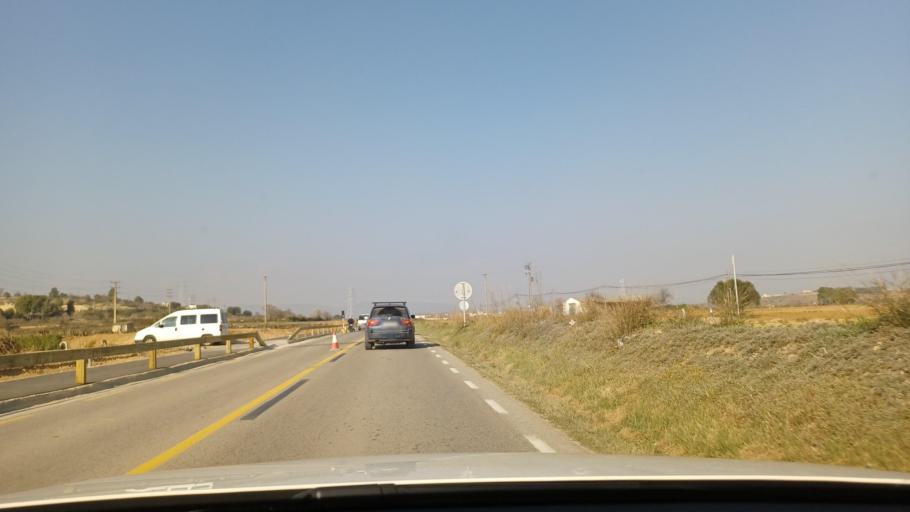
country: ES
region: Catalonia
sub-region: Provincia de Barcelona
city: Vilafranca del Penedes
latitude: 41.3625
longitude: 1.6950
